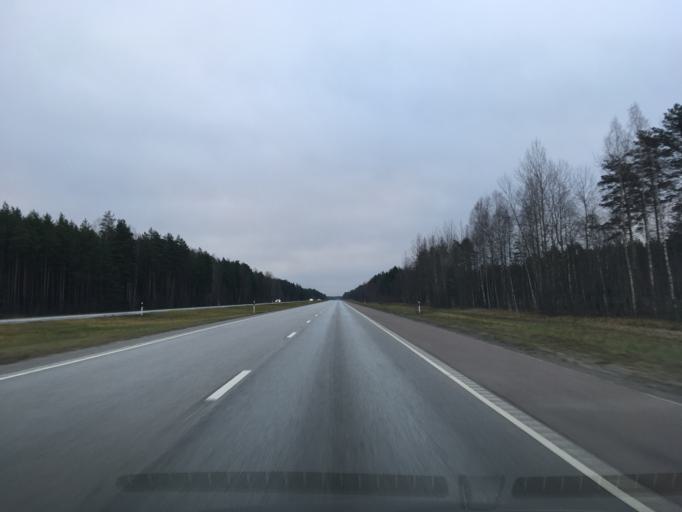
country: EE
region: Harju
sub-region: Kuusalu vald
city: Kuusalu
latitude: 59.4512
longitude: 25.4659
